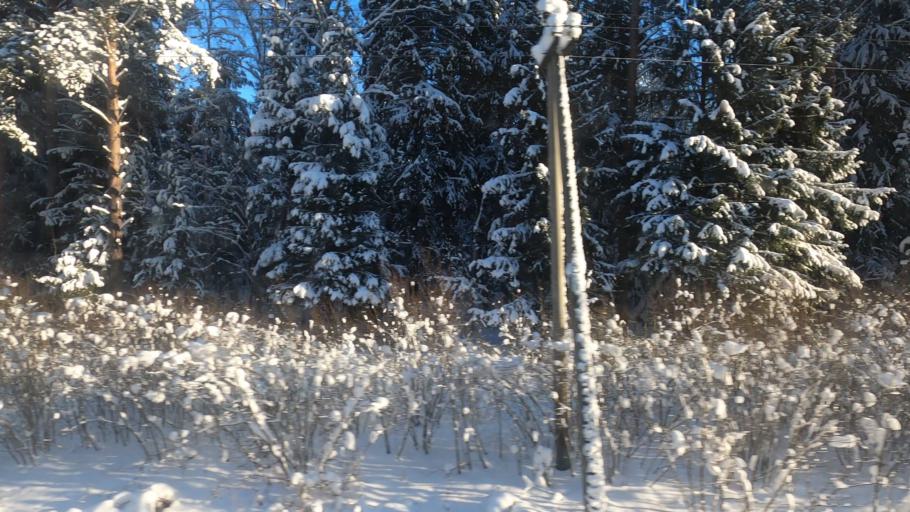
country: RU
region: Moskovskaya
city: Novo-Nikol'skoye
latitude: 56.5577
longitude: 37.5654
